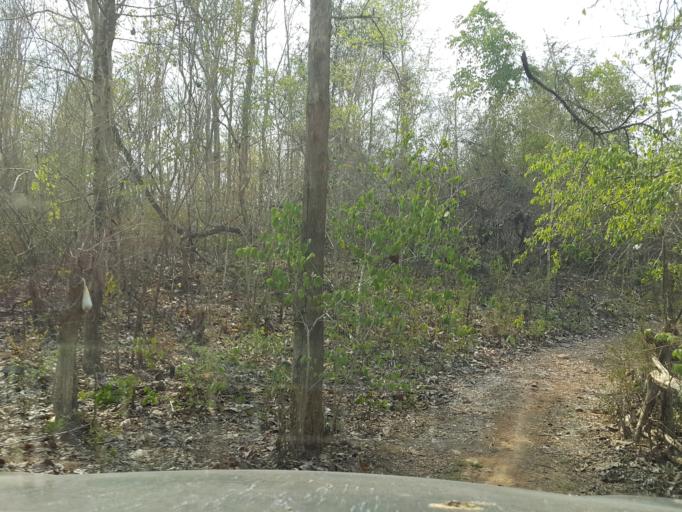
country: TH
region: Lampang
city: Mae Phrik
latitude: 17.5258
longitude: 98.9932
